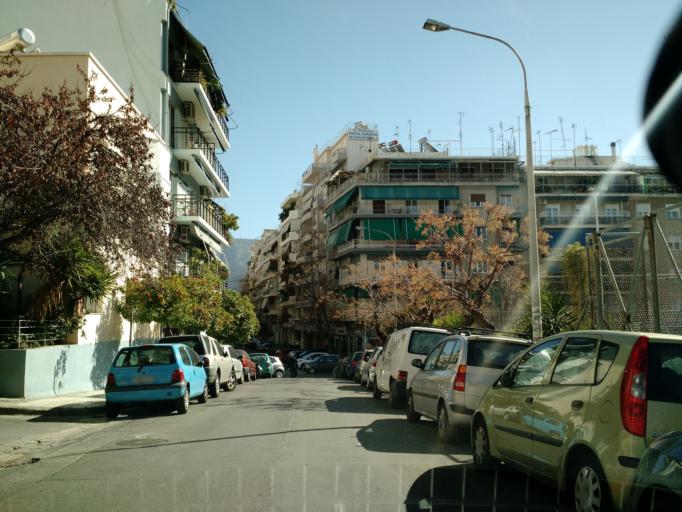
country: GR
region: Attica
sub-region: Nomarchia Athinas
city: Psychiko
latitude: 37.9898
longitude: 23.7618
